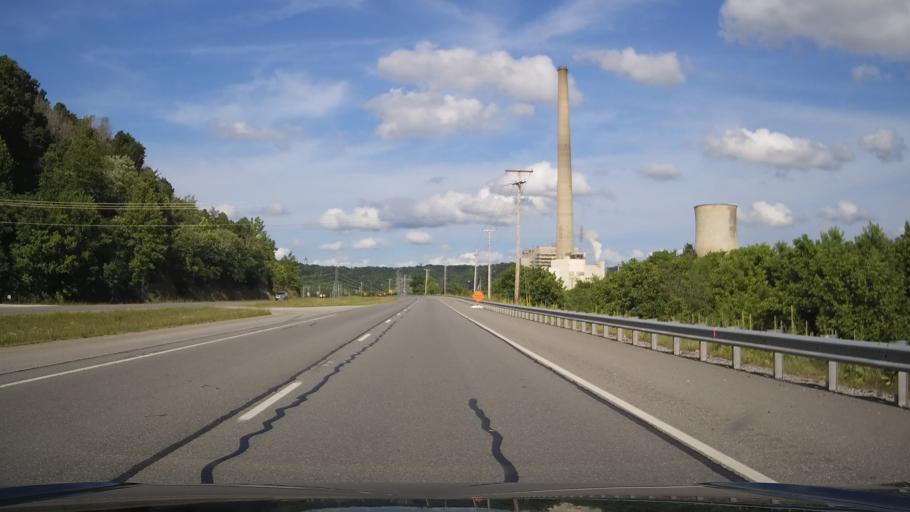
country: US
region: Kentucky
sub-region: Lawrence County
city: Louisa
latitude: 38.1716
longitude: -82.6277
